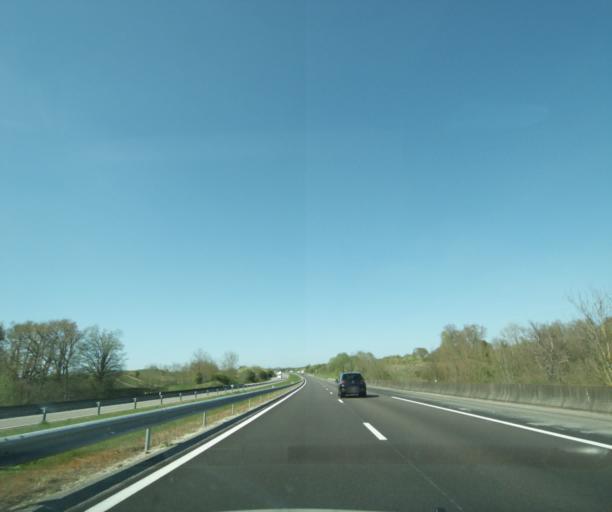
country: FR
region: Bourgogne
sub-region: Departement de la Nievre
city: Cosne-Cours-sur-Loire
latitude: 47.4781
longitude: 2.9446
